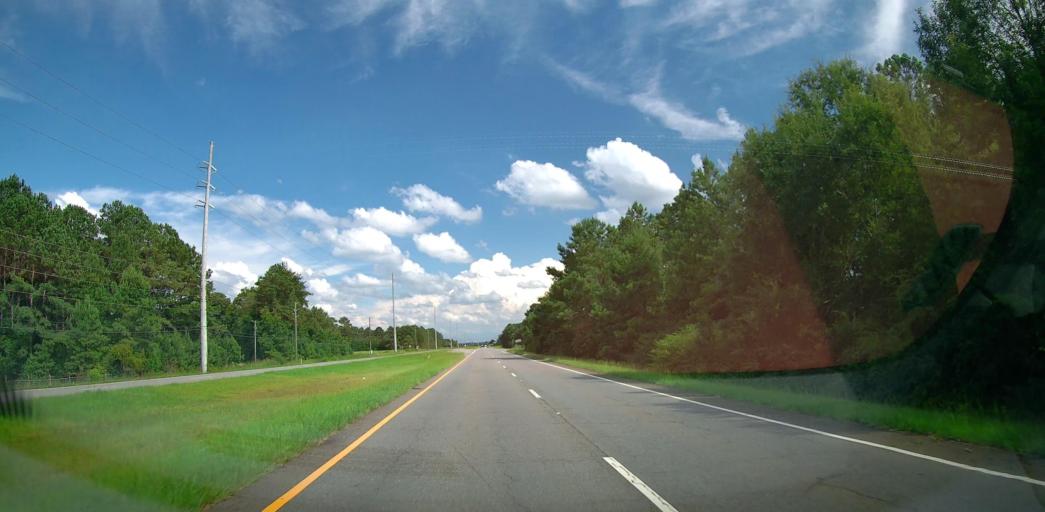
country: US
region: Georgia
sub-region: Houston County
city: Perry
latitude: 32.4824
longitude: -83.7125
